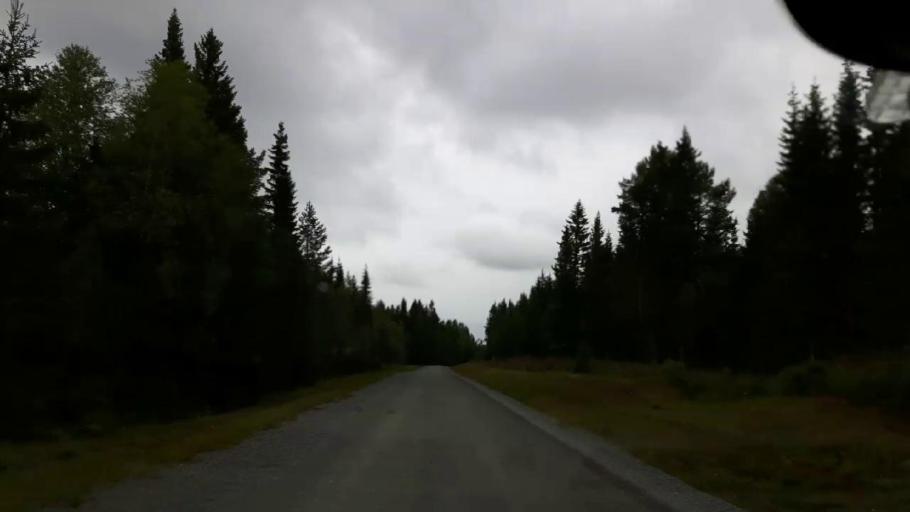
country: SE
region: Jaemtland
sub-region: OEstersunds Kommun
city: Ostersund
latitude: 63.0691
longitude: 14.5530
